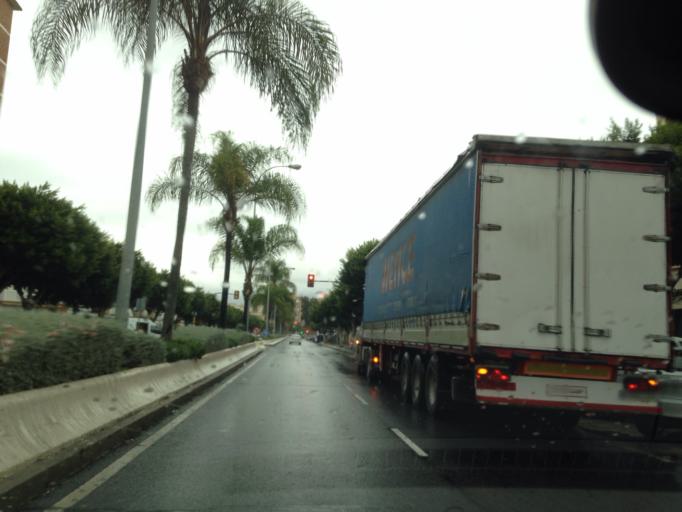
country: ES
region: Andalusia
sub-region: Provincia de Malaga
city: Malaga
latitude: 36.6966
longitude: -4.4420
